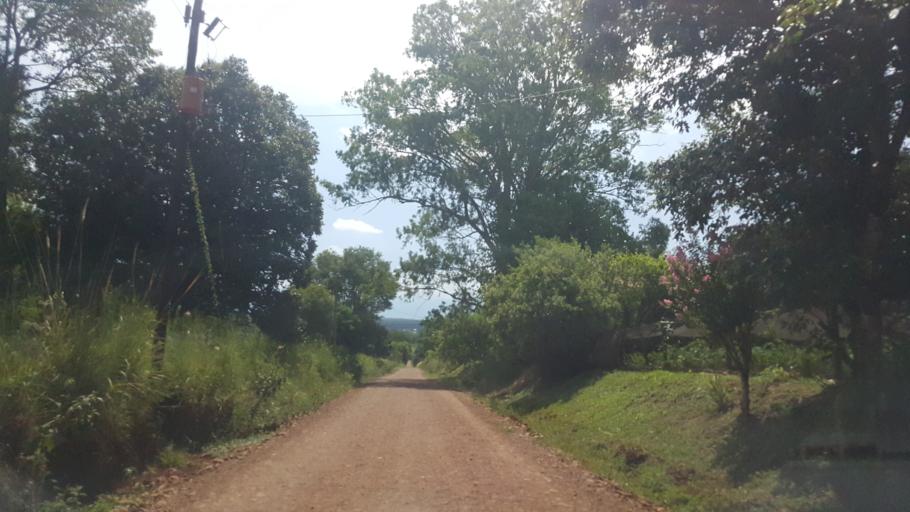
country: AR
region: Misiones
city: Capiovi
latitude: -26.9257
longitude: -55.0426
